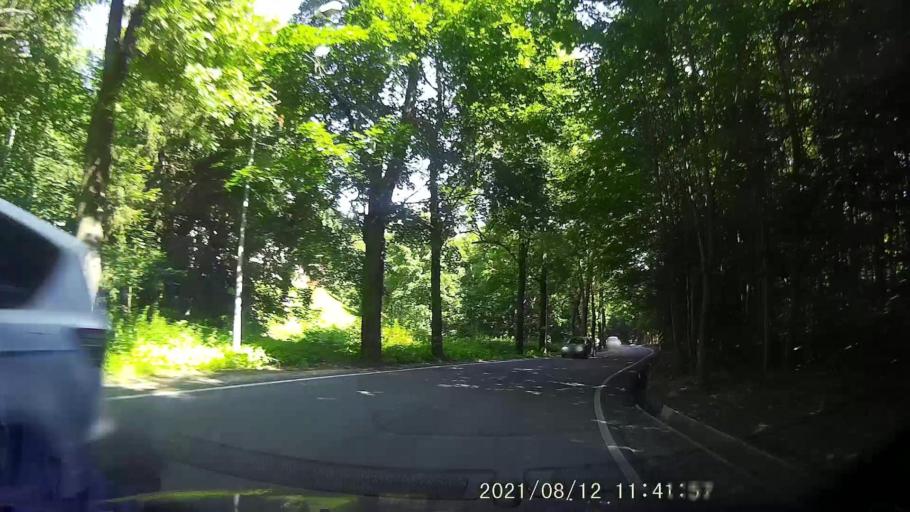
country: PL
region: Lower Silesian Voivodeship
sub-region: Powiat klodzki
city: Stronie Slaskie
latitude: 50.2614
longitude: 16.8235
